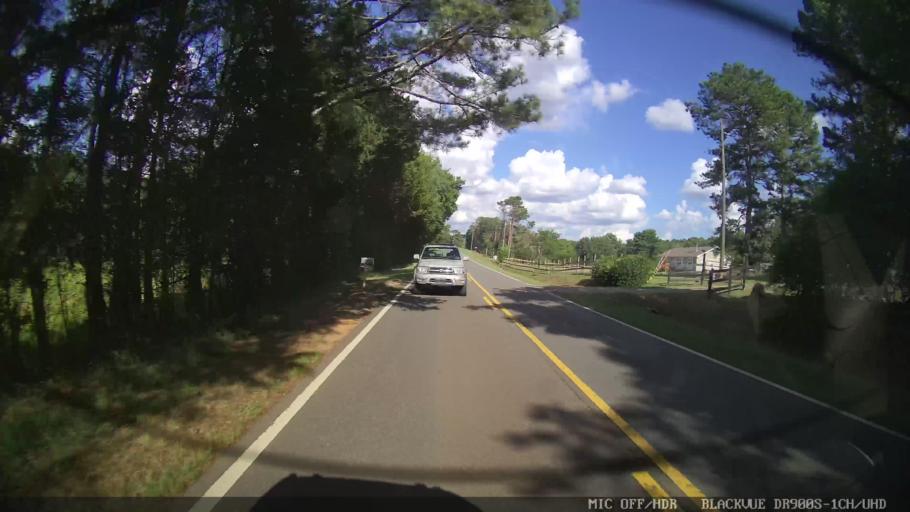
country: US
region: Georgia
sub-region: Bartow County
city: Euharlee
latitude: 34.1796
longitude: -85.0239
